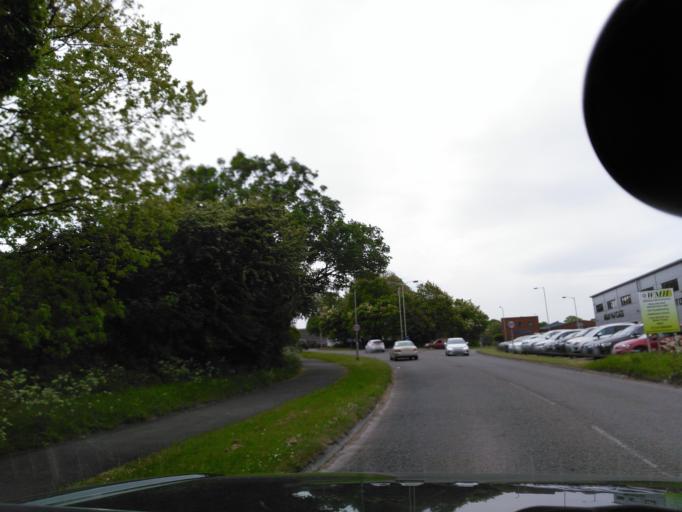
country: GB
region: England
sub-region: Wiltshire
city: Melksham
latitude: 51.3612
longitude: -2.1285
